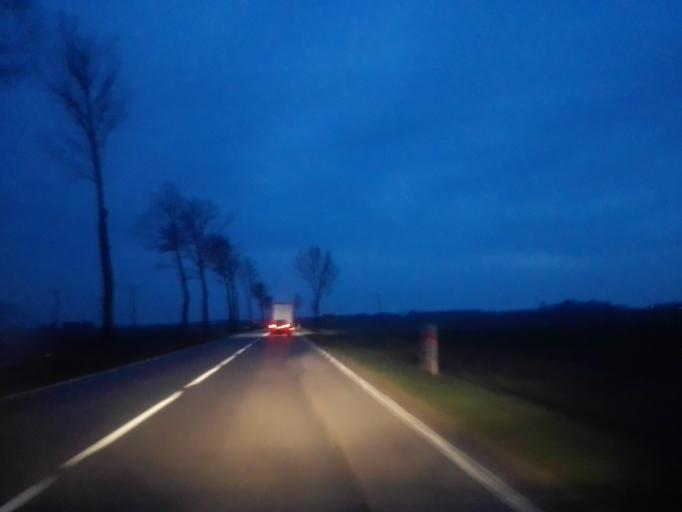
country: PL
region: Podlasie
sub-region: Powiat lomzynski
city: Sniadowo
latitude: 53.0870
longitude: 22.0207
